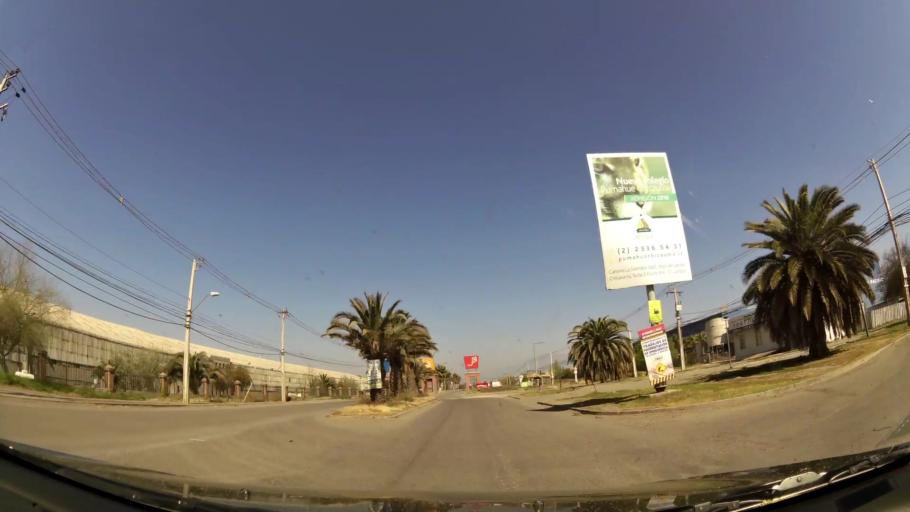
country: CL
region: Santiago Metropolitan
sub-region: Provincia de Chacabuco
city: Chicureo Abajo
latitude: -33.3153
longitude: -70.7281
